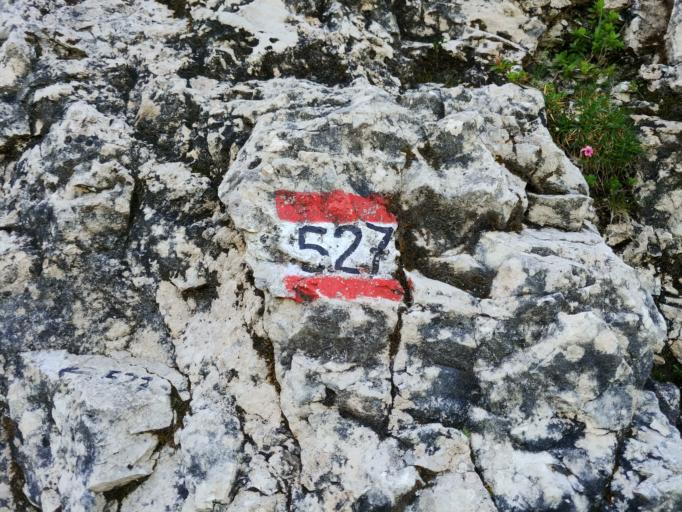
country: IT
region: Trentino-Alto Adige
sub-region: Bolzano
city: Santa Cristina Valgardena
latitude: 46.5226
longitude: 11.7106
